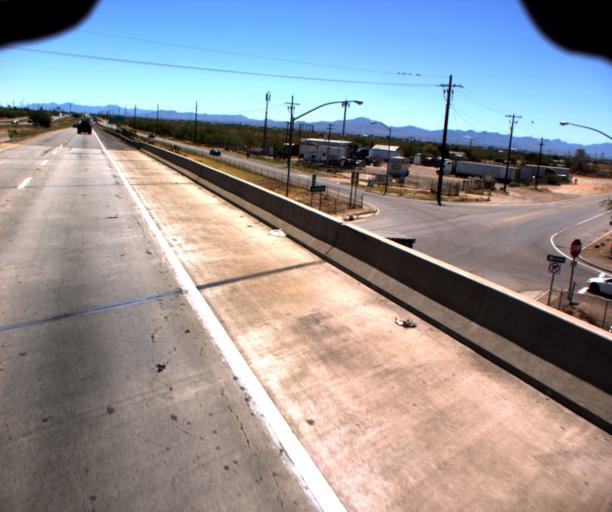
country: US
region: Arizona
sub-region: Pima County
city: Summit
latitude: 32.1253
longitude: -110.8754
